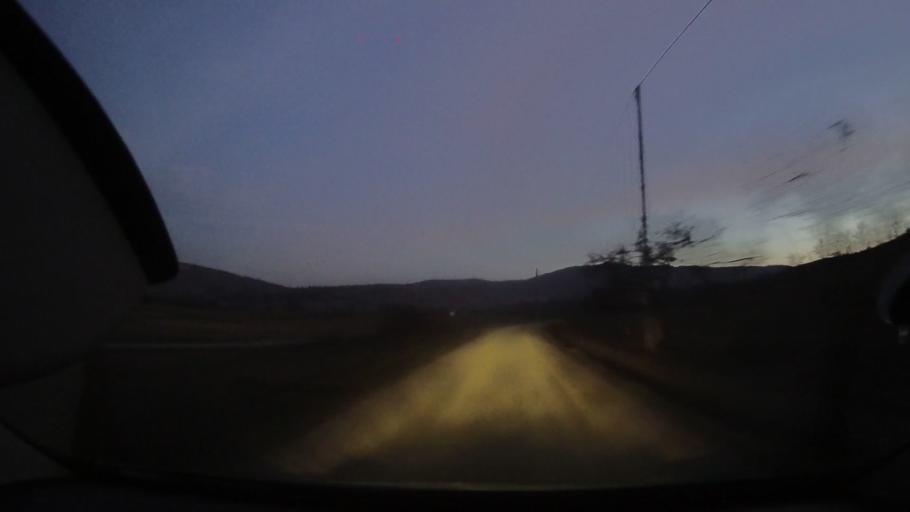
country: RO
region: Bihor
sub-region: Comuna Varciorog
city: Varciorog
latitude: 46.9884
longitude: 22.3268
